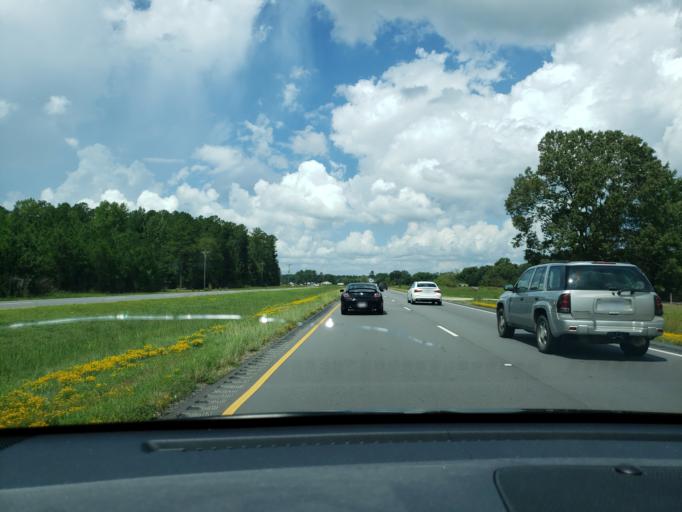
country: US
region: North Carolina
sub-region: Robeson County
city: Saint Pauls
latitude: 34.7877
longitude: -78.8137
